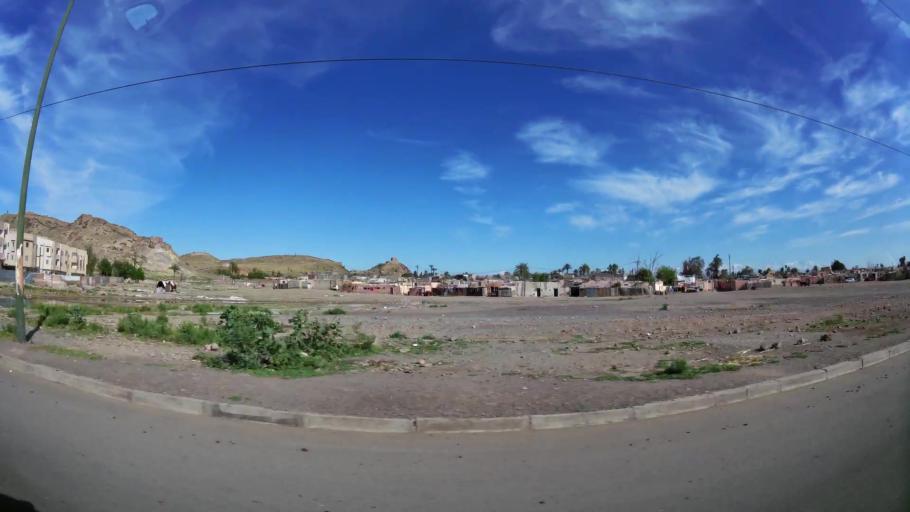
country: MA
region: Marrakech-Tensift-Al Haouz
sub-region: Marrakech
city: Marrakesh
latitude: 31.6466
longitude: -8.0382
